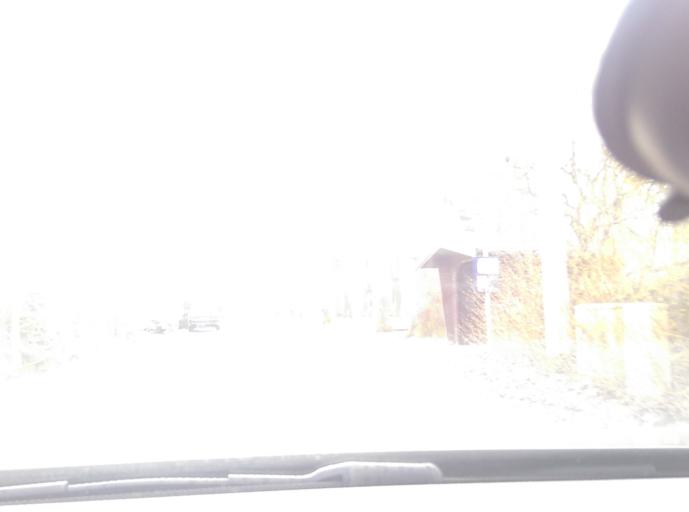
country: DE
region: Lower Saxony
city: Lindwedel
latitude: 52.5722
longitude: 9.5997
